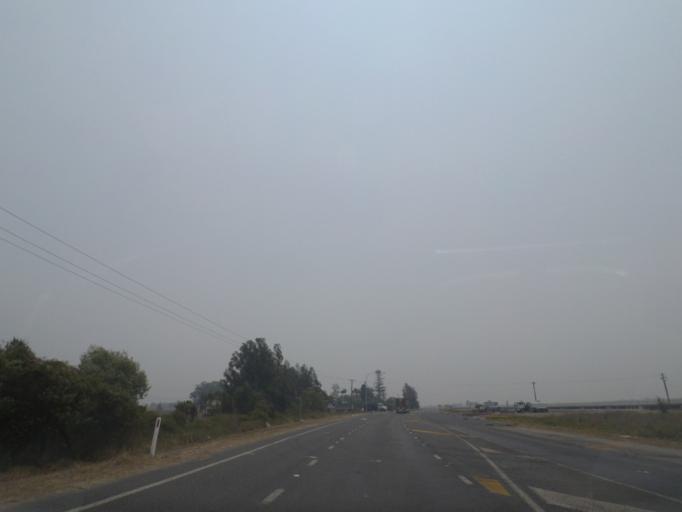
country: AU
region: New South Wales
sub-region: Clarence Valley
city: Maclean
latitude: -29.4205
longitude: 153.2409
